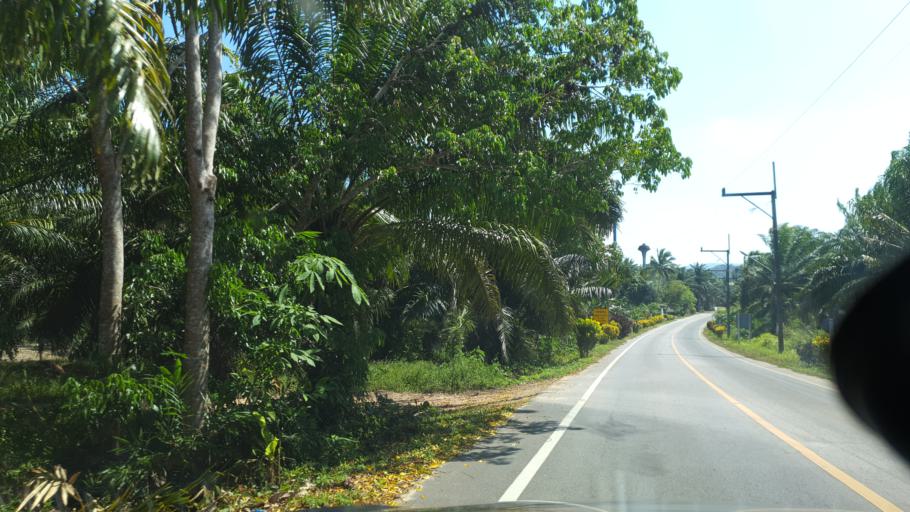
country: TH
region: Krabi
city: Khlong Thom
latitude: 7.9387
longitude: 99.2179
